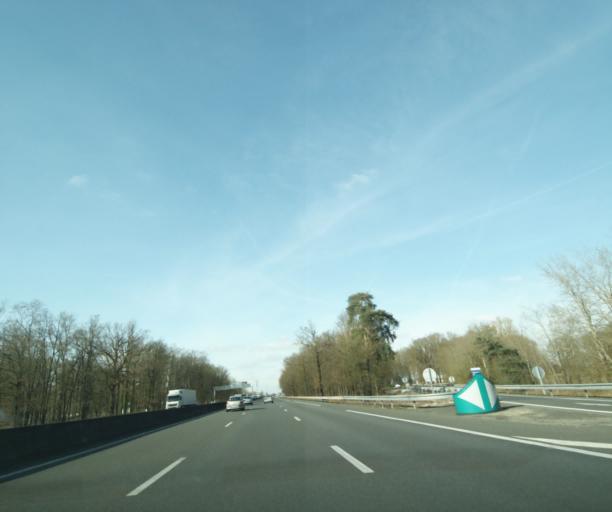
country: FR
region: Centre
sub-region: Departement du Loiret
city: Artenay
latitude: 48.1070
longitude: 1.8512
